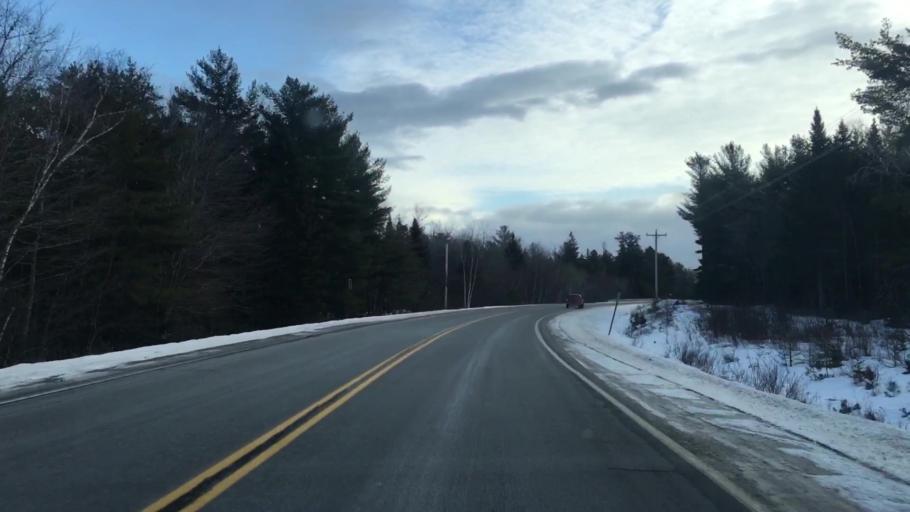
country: US
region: Maine
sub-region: Washington County
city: Machias
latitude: 45.0000
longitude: -67.6023
